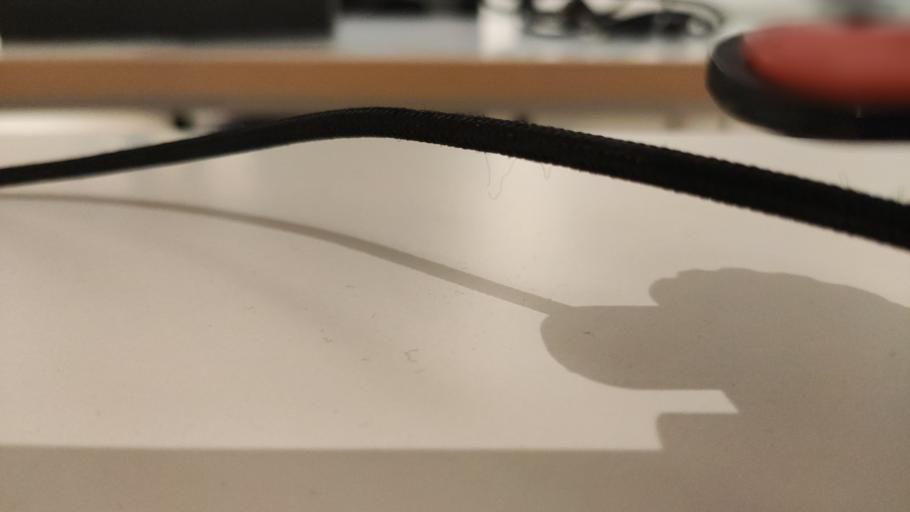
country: RU
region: Moskovskaya
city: Dorokhovo
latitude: 55.5171
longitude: 36.3523
